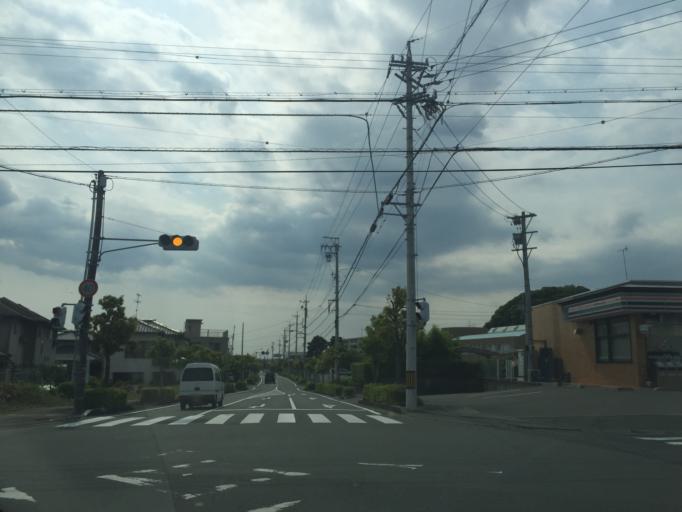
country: JP
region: Shizuoka
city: Kakegawa
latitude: 34.7809
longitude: 138.0201
